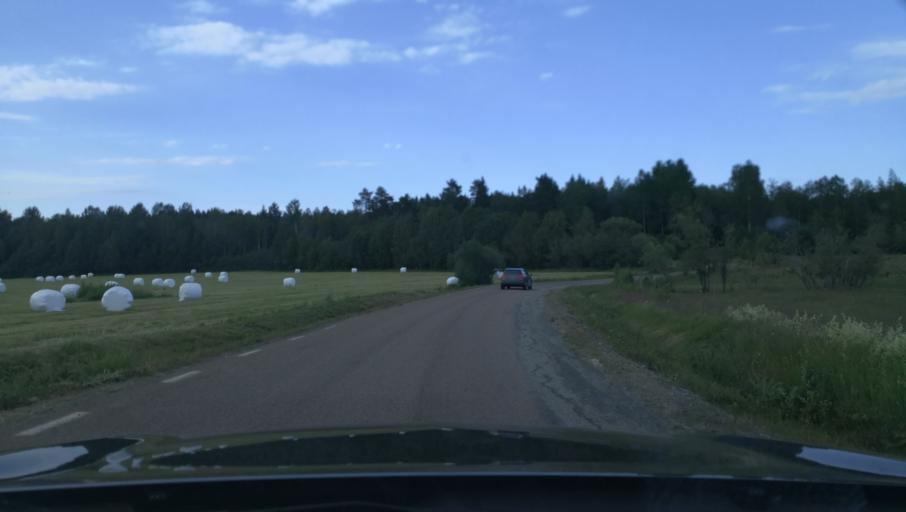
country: SE
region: Dalarna
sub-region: Ludvika Kommun
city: Ludvika
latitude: 60.0774
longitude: 15.2576
